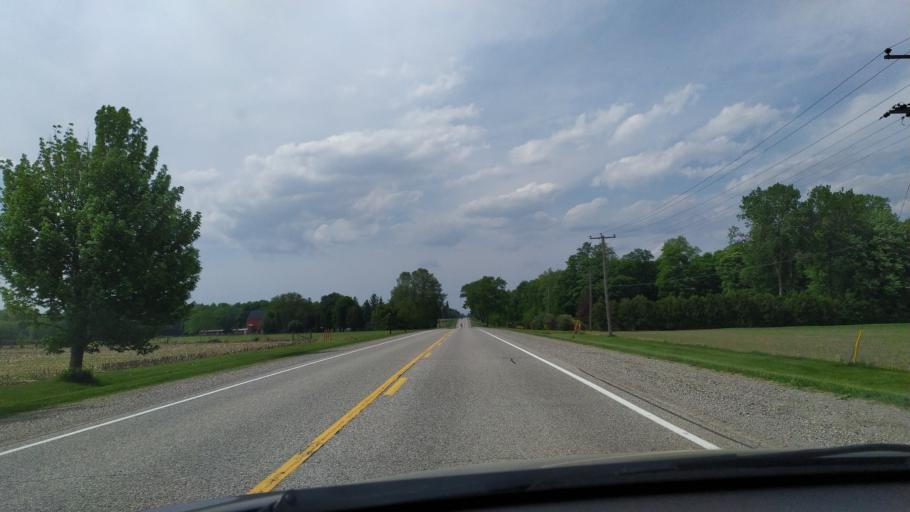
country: CA
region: Ontario
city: Dorchester
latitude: 43.0910
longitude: -81.0056
